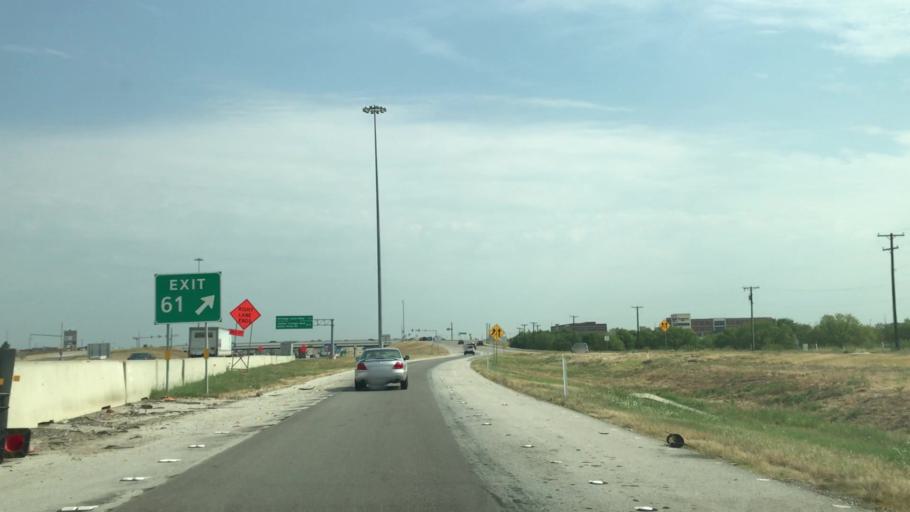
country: US
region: Texas
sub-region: Tarrant County
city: Blue Mound
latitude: 32.8941
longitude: -97.3169
